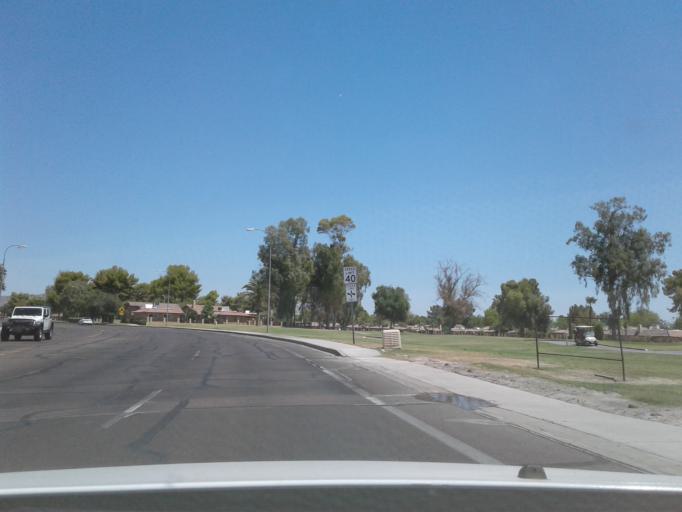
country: US
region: Arizona
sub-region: Maricopa County
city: Guadalupe
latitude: 33.3325
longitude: -111.9808
